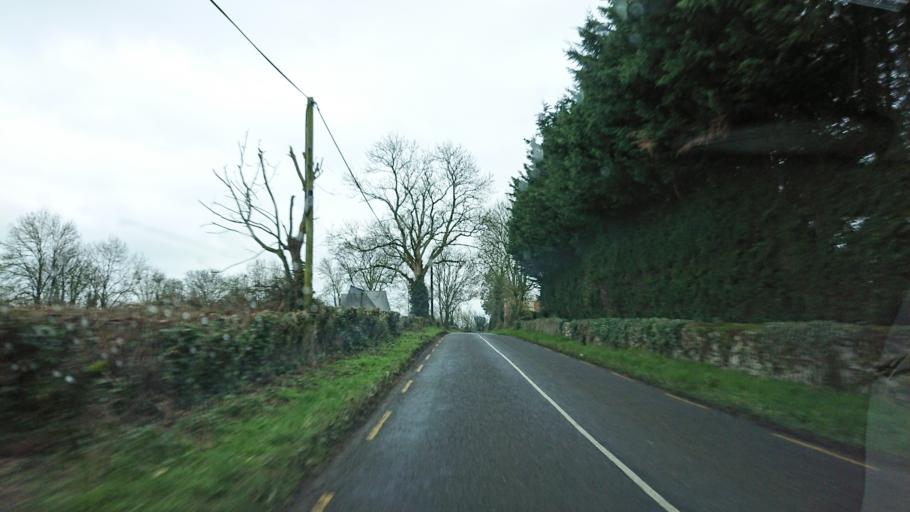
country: IE
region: Leinster
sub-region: Kilkenny
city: Callan
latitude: 52.5349
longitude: -7.2928
